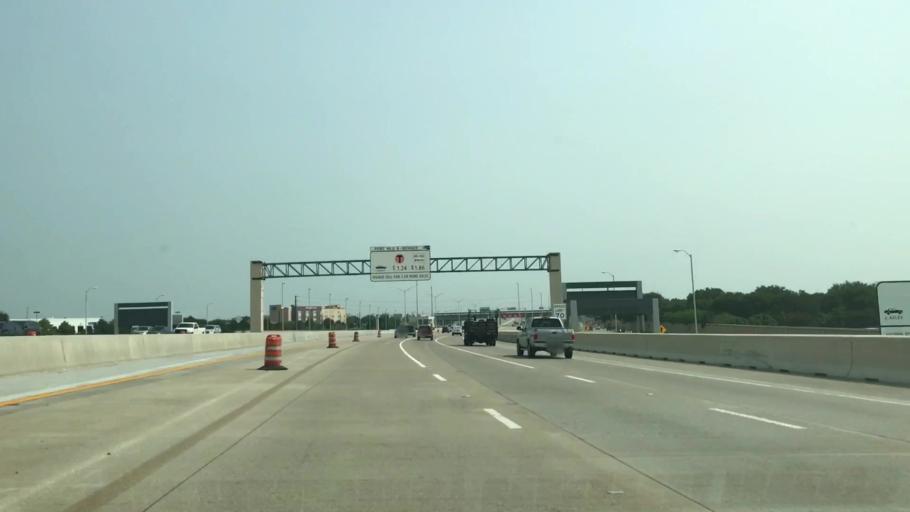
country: US
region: Texas
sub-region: Collin County
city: Plano
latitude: 32.9948
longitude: -96.6693
